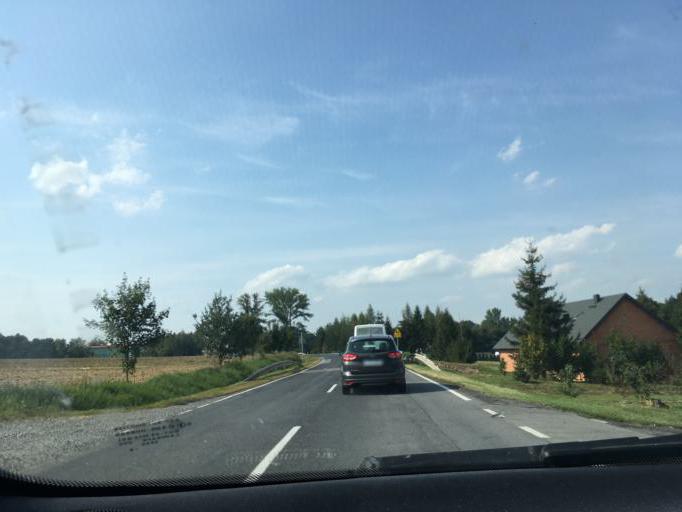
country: PL
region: Opole Voivodeship
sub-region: Powiat prudnicki
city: Laka Prudnicka
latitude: 50.3772
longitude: 17.5330
